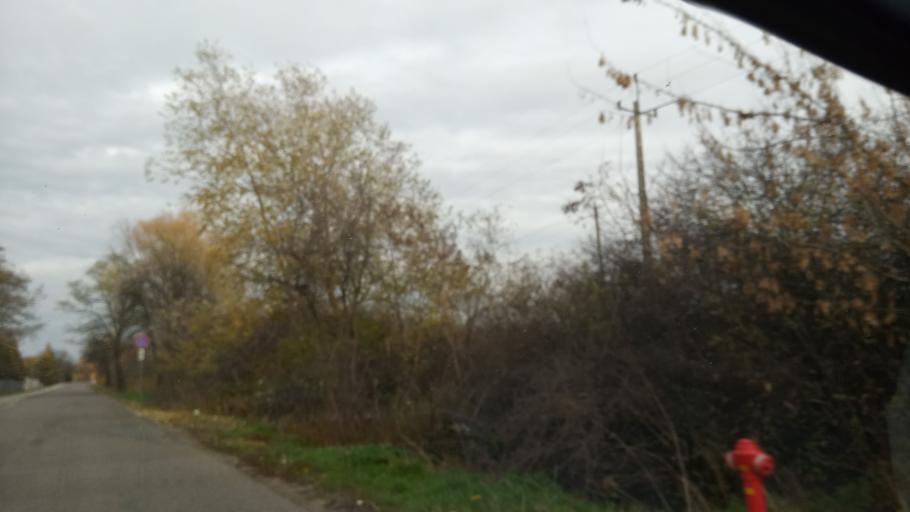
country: PL
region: Lodz Voivodeship
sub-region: Powiat skierniewicki
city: Bolimow
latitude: 52.1608
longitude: 20.1703
